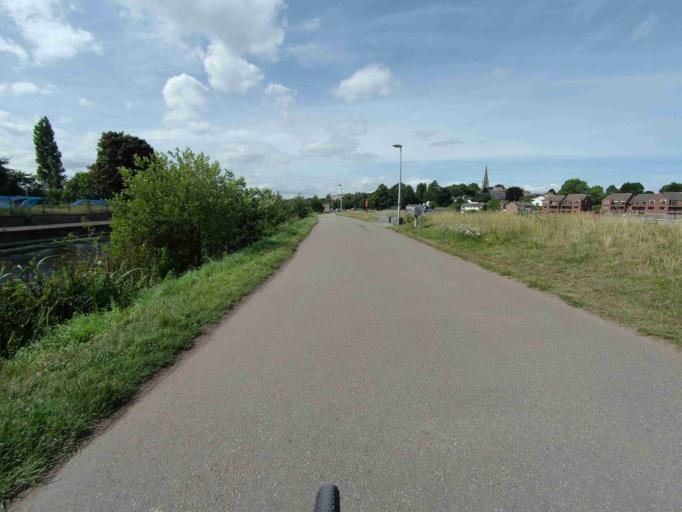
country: GB
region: England
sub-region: Devon
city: Exeter
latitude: 50.7134
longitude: -3.5263
